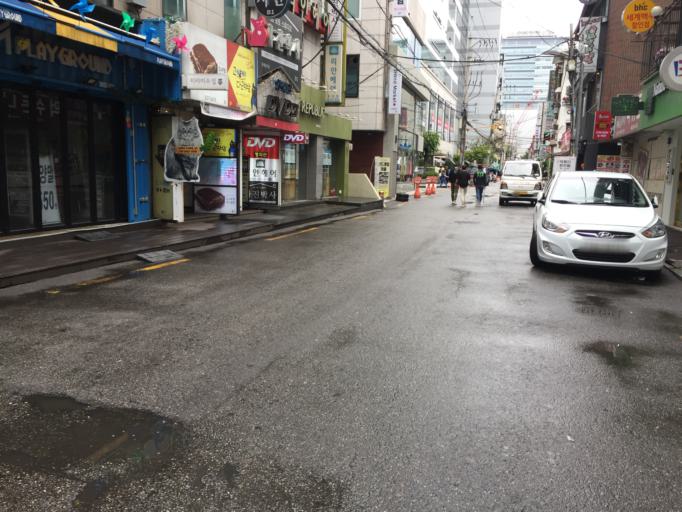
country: KR
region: Seoul
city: Seoul
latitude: 37.5553
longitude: 126.9230
